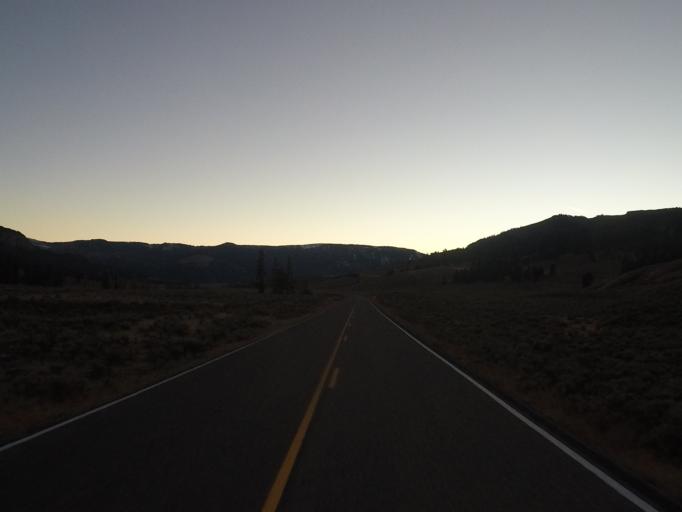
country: US
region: Montana
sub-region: Park County
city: Livingston
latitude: 44.8948
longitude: -110.1293
